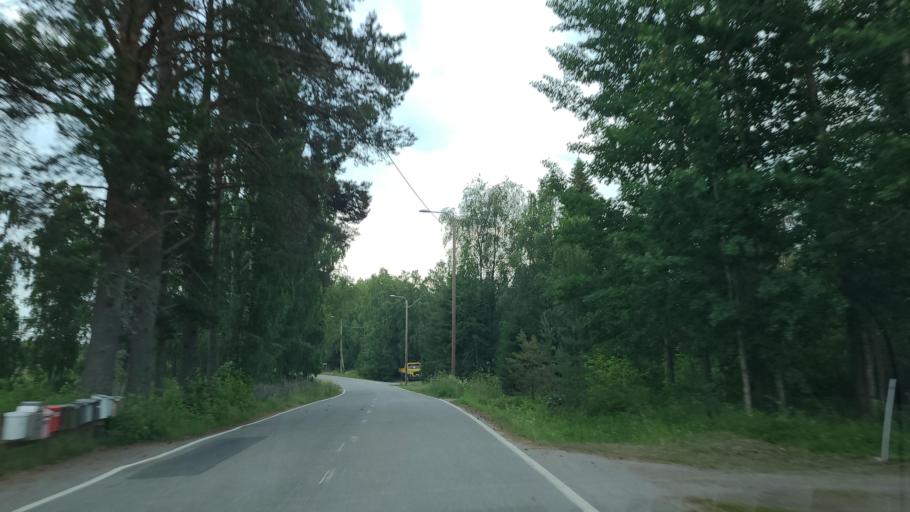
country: FI
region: Ostrobothnia
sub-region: Vaasa
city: Replot
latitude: 63.1680
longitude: 21.2606
